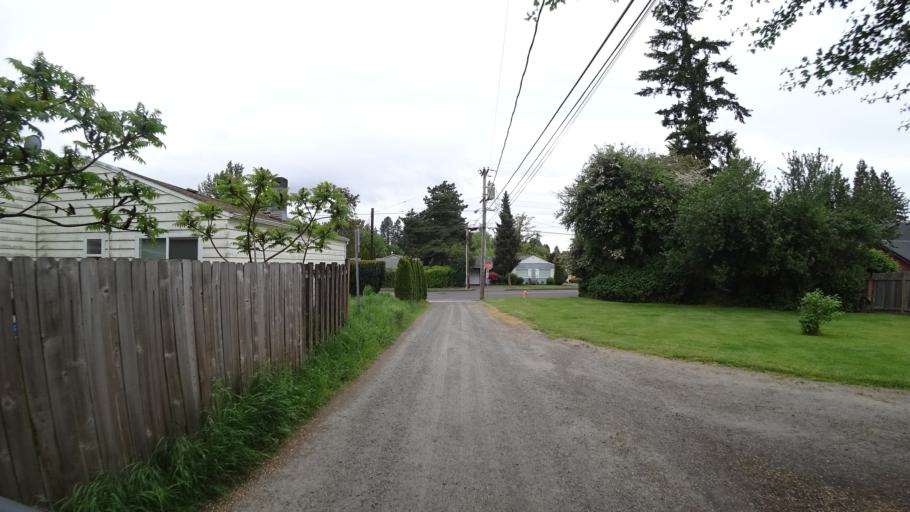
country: US
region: Oregon
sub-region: Washington County
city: Beaverton
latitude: 45.4772
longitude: -122.8068
